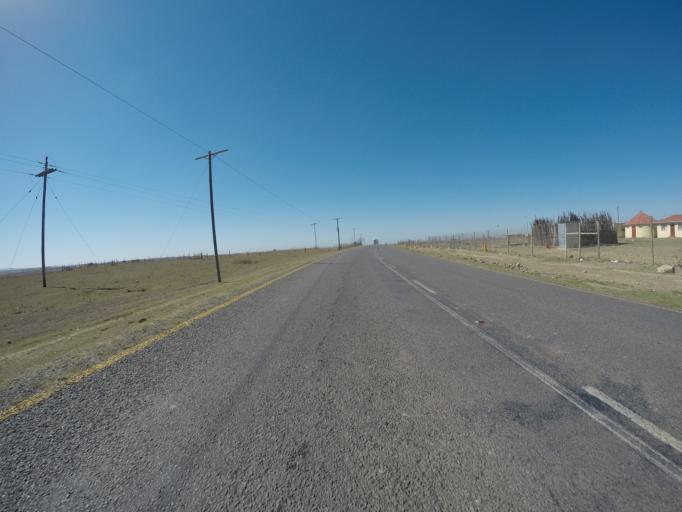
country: ZA
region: Eastern Cape
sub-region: OR Tambo District Municipality
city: Mthatha
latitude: -31.8874
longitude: 28.7621
